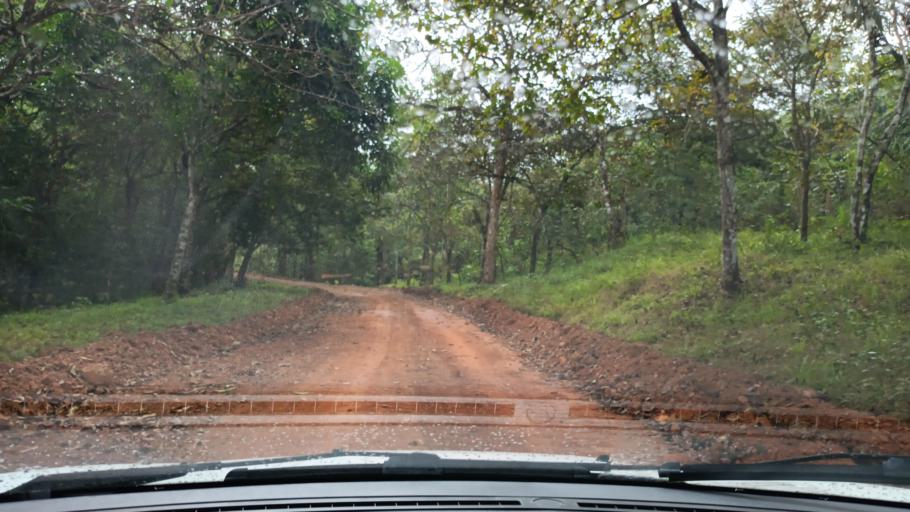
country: PA
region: Panama
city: La Cabima
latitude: 9.1273
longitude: -79.5105
